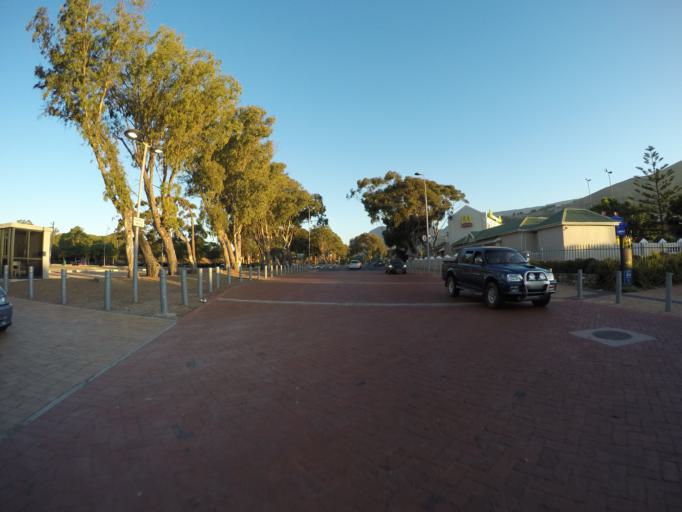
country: ZA
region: Western Cape
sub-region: City of Cape Town
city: Cape Town
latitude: -33.9057
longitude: 18.4108
